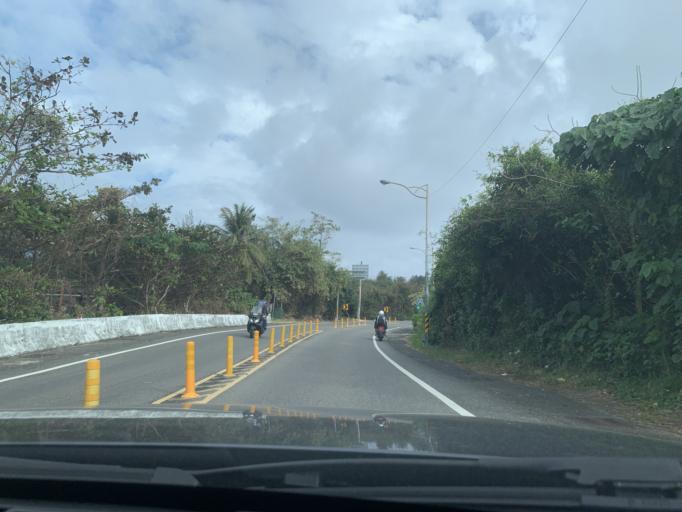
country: TW
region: Taiwan
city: Hengchun
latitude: 21.9051
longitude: 120.8523
